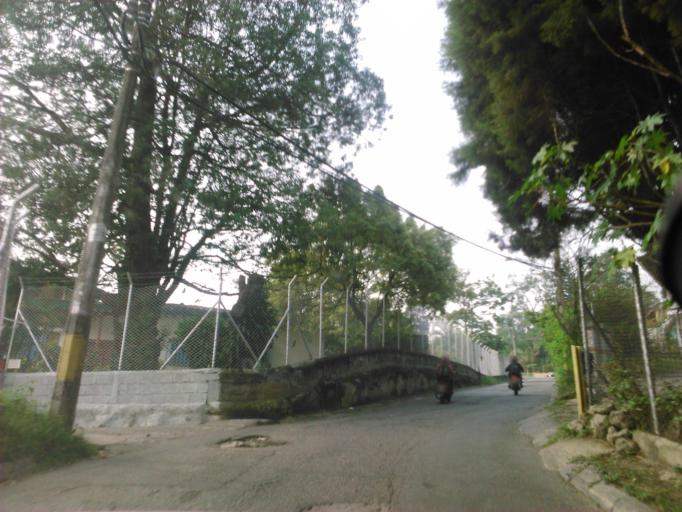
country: CO
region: Antioquia
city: La Estrella
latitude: 6.1468
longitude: -75.6355
